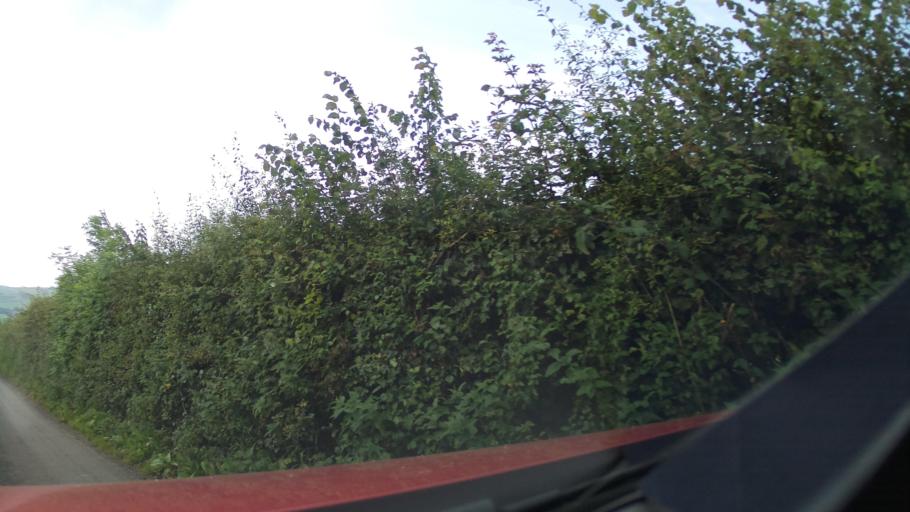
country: GB
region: England
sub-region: Somerset
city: Evercreech
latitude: 51.1447
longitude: -2.4892
